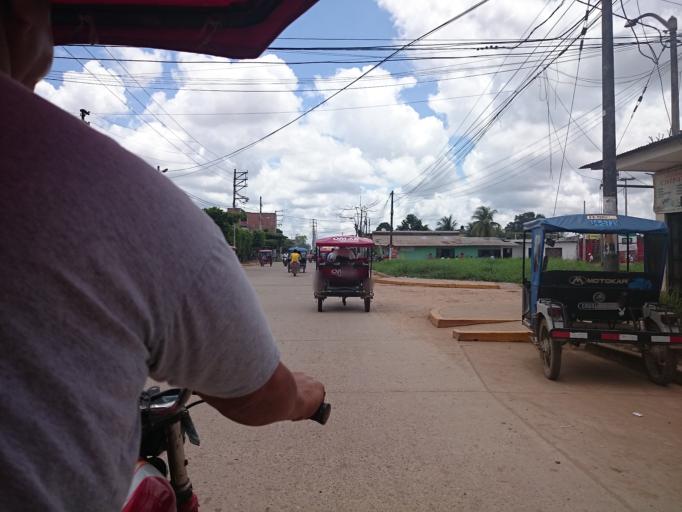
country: PE
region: Ucayali
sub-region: Provincia de Coronel Portillo
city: Pucallpa
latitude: -8.3818
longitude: -74.5479
